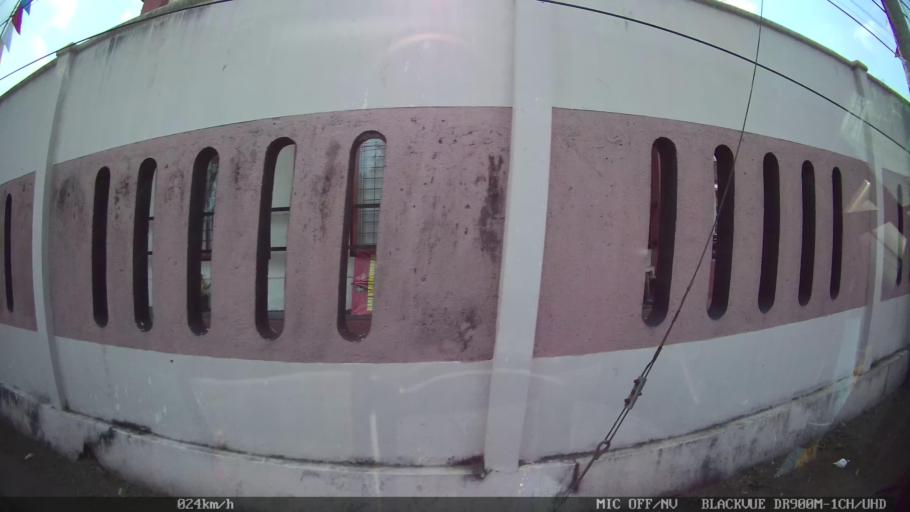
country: ID
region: Daerah Istimewa Yogyakarta
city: Yogyakarta
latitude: -7.8170
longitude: 110.4008
